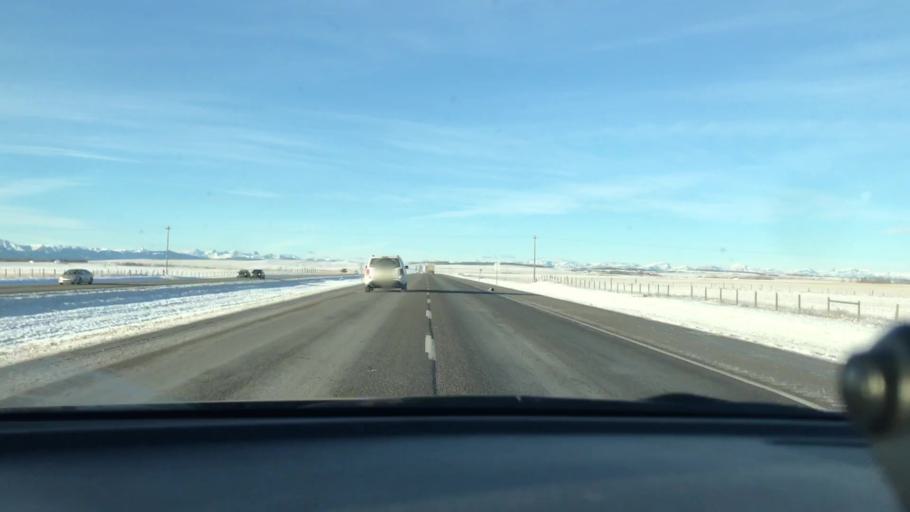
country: CA
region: Alberta
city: Cochrane
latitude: 51.0895
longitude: -114.3731
